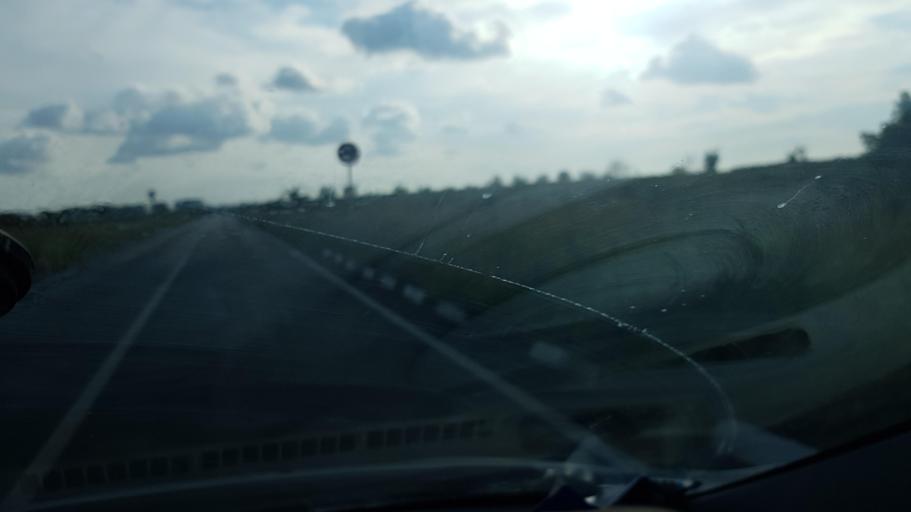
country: IT
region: Apulia
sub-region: Provincia di Brindisi
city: San Donaci
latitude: 40.4379
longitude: 17.9542
